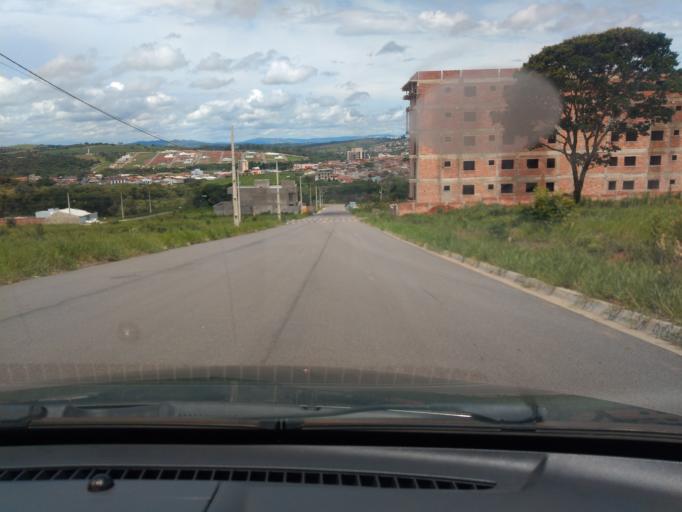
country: BR
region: Minas Gerais
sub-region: Tres Coracoes
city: Tres Coracoes
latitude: -21.6786
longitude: -45.2769
